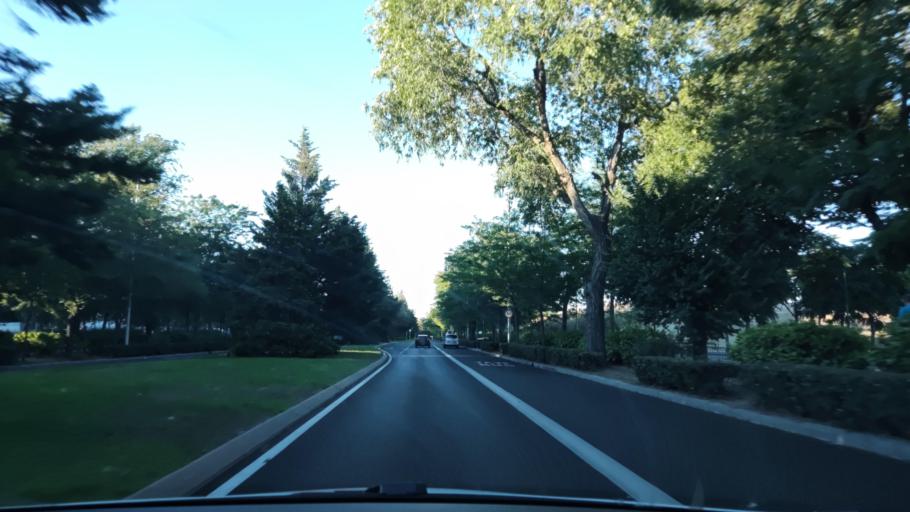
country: ES
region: Madrid
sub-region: Provincia de Madrid
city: Carabanchel
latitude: 40.3798
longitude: -3.7264
